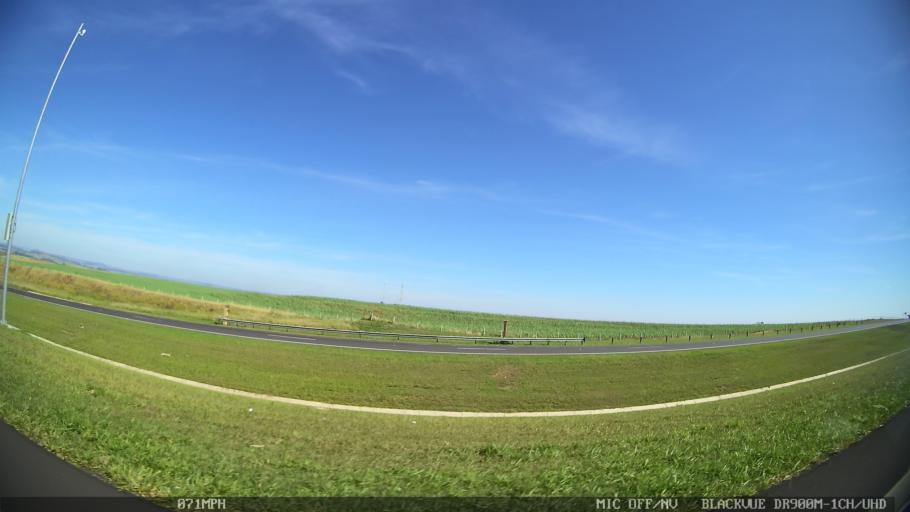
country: BR
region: Sao Paulo
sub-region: Santa Rita Do Passa Quatro
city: Santa Rita do Passa Quatro
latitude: -21.6995
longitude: -47.5963
